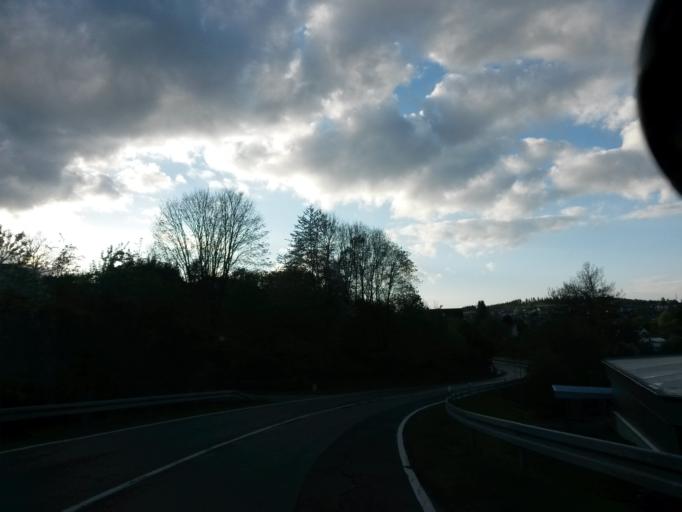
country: DE
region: North Rhine-Westphalia
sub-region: Regierungsbezirk Arnsberg
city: Herscheid
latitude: 51.1719
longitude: 7.7518
